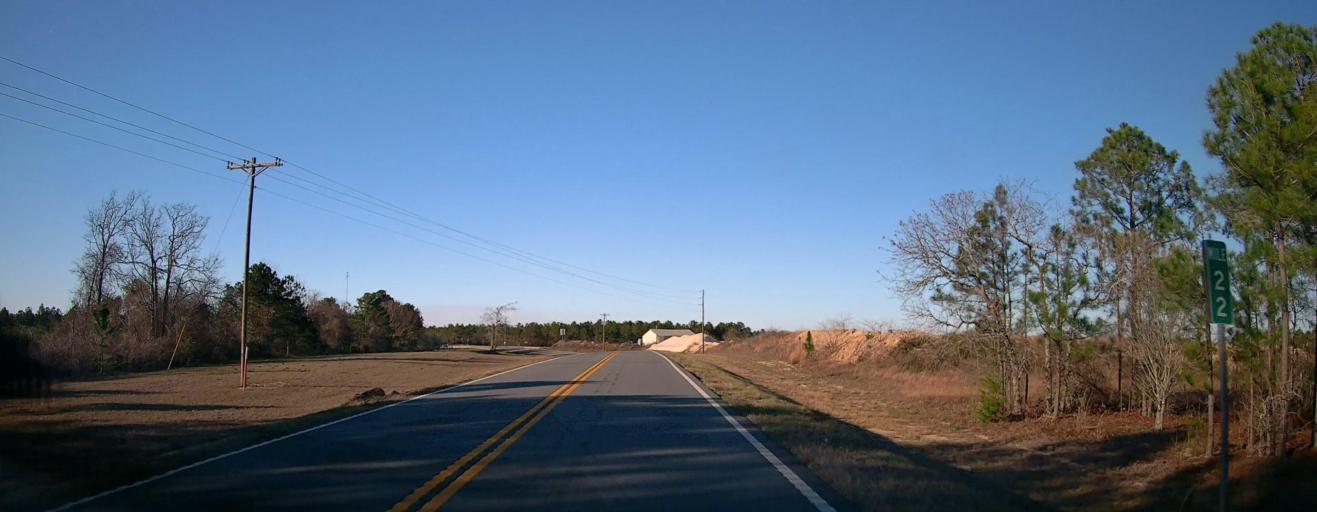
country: US
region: Georgia
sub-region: Talbot County
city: Talbotton
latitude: 32.5592
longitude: -84.4371
